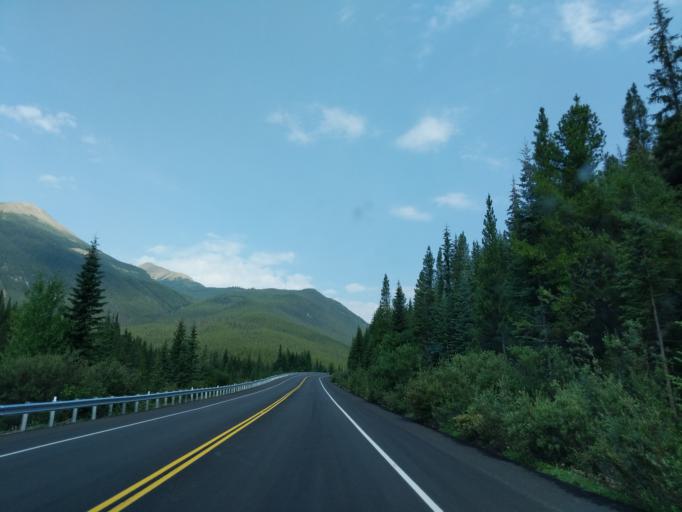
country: CA
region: British Columbia
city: Golden
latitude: 52.1169
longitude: -116.9783
